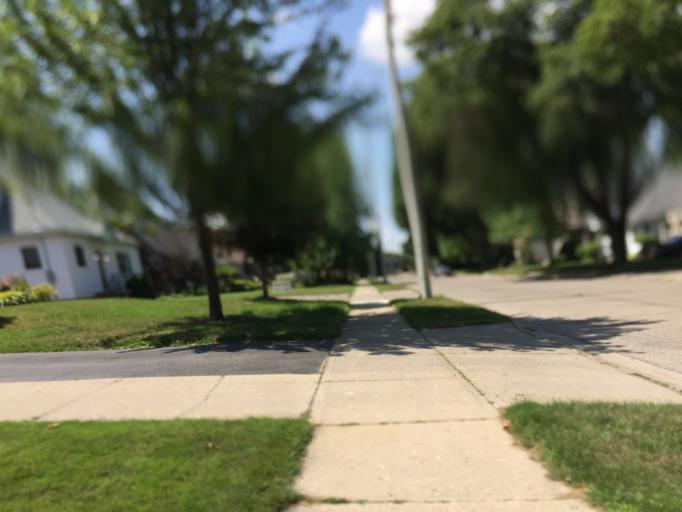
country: CA
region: Ontario
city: Stratford
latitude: 43.3781
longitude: -80.9900
